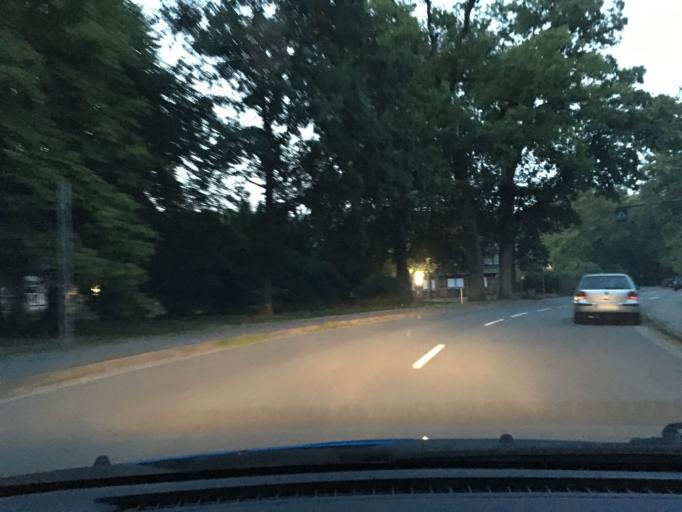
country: DE
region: Lower Saxony
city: Bispingen
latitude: 53.0163
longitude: 9.9591
